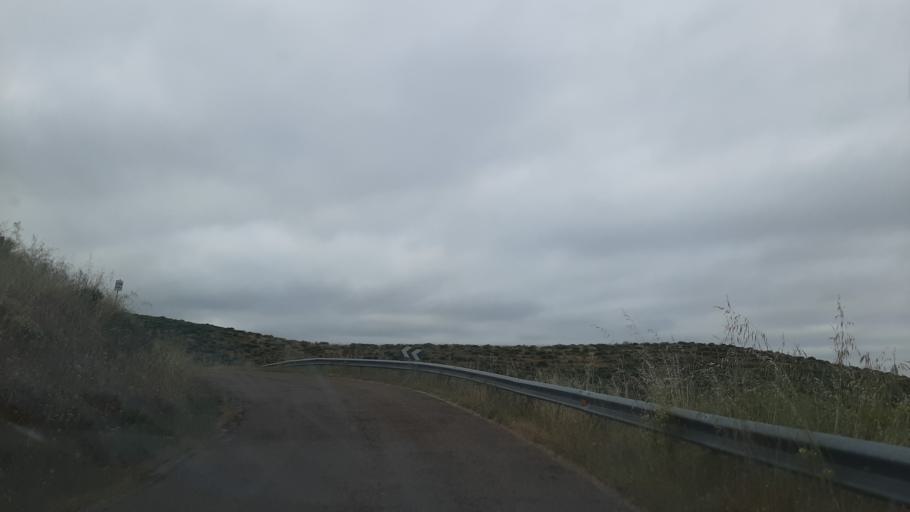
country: ES
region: Castille and Leon
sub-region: Provincia de Salamanca
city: Zamarra
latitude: 40.5280
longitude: -6.4711
